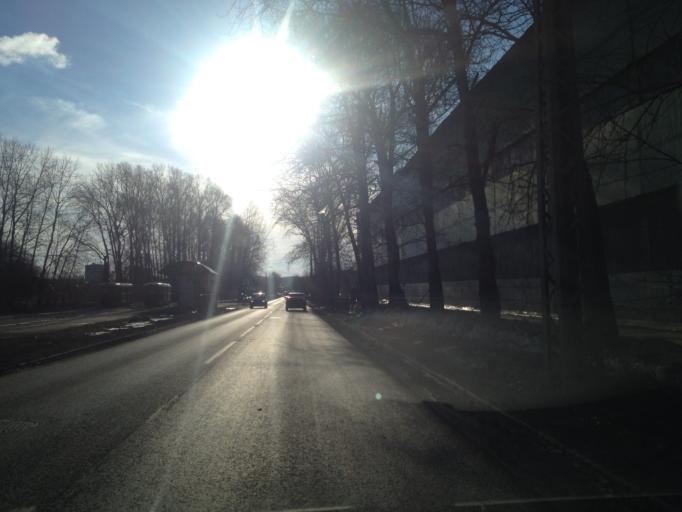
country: RU
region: Sverdlovsk
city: Sovkhoznyy
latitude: 56.7569
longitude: 60.5946
